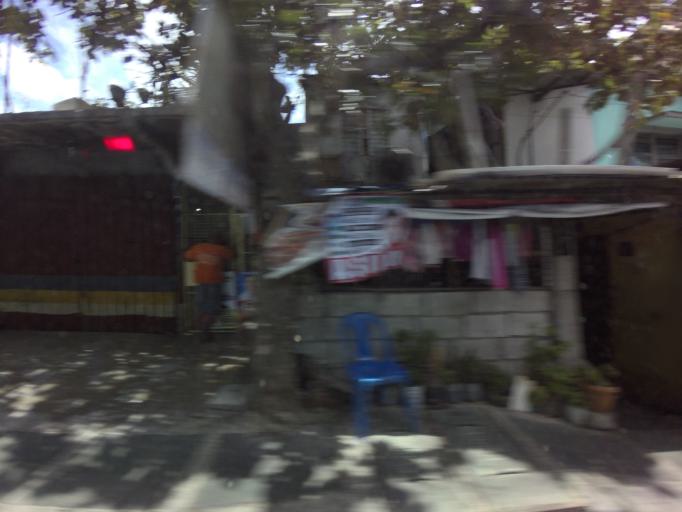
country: PH
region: Metro Manila
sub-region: Marikina
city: Calumpang
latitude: 14.6007
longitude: 121.0925
